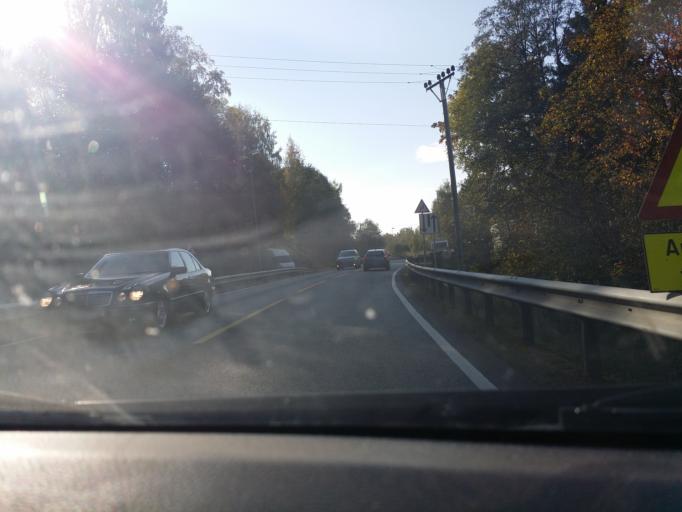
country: NO
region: Buskerud
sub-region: Hole
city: Vik
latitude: 60.0581
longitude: 10.3044
